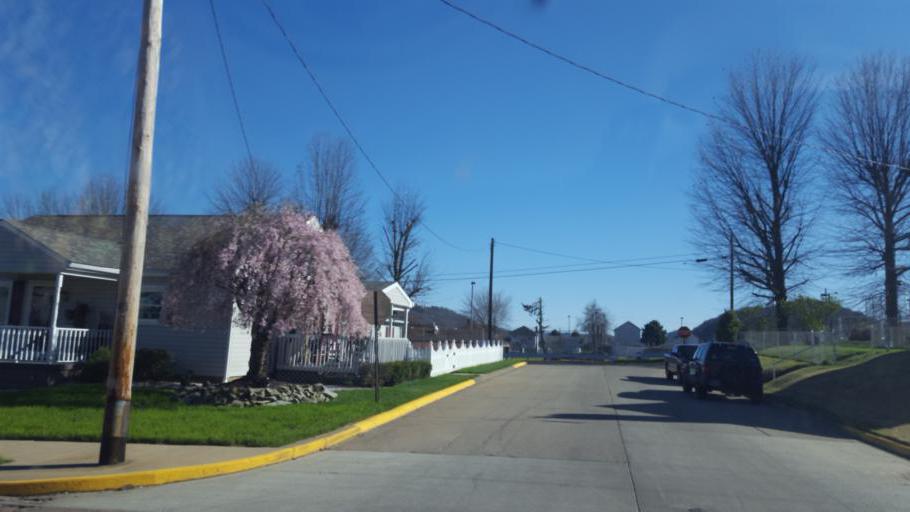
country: US
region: Ohio
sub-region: Jefferson County
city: Toronto
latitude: 40.4614
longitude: -80.6087
